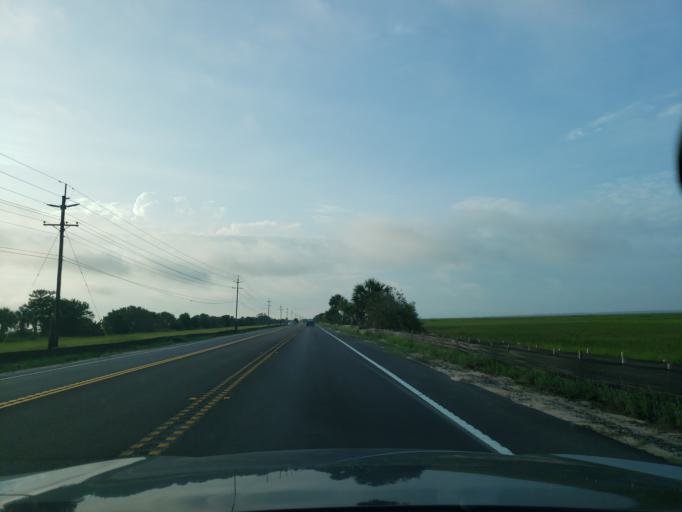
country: US
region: Georgia
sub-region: Chatham County
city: Wilmington Island
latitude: 32.0337
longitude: -80.9352
